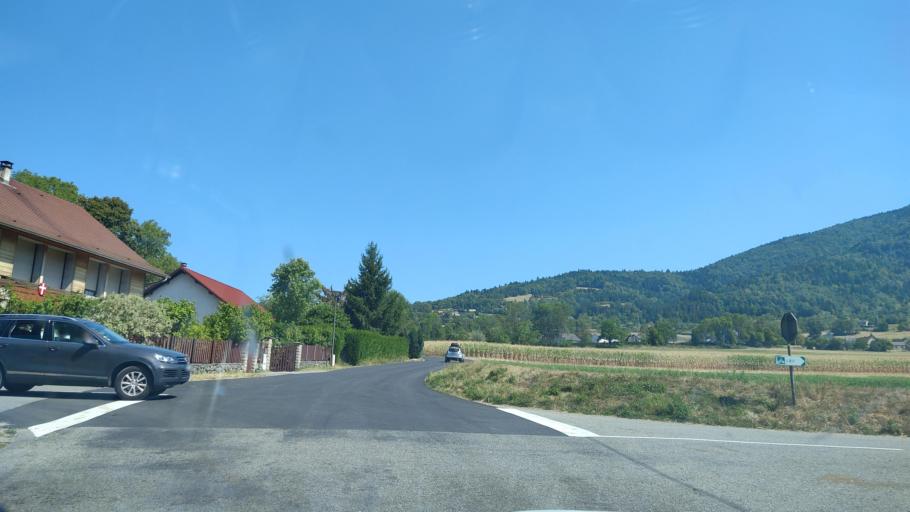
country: FR
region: Rhone-Alpes
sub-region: Departement de la Savoie
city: Novalaise
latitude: 45.5954
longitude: 5.7783
